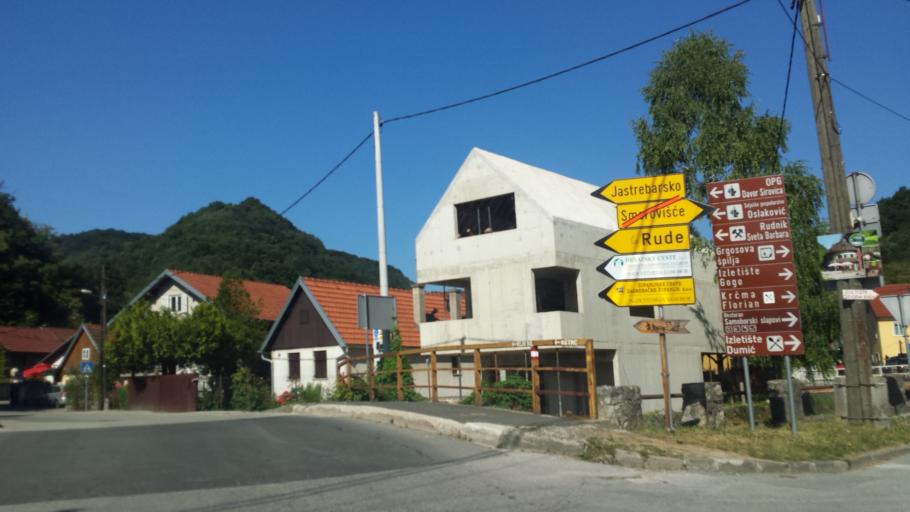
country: HR
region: Zagrebacka
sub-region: Grad Samobor
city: Samobor
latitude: 45.8008
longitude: 15.6994
